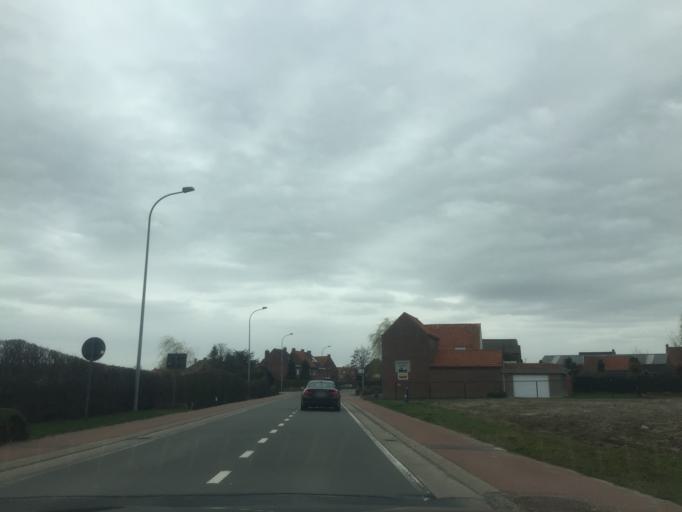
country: BE
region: Flanders
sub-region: Provincie West-Vlaanderen
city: Izegem
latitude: 50.9326
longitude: 3.2108
